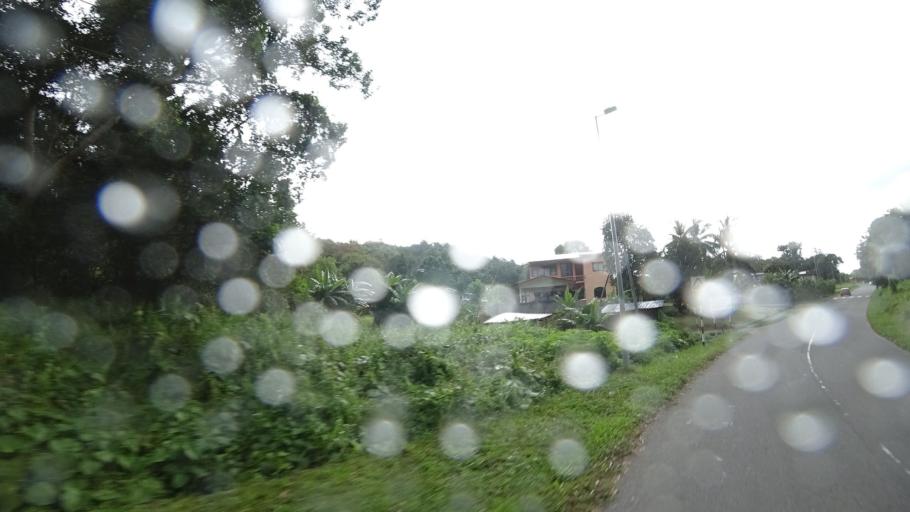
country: BN
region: Brunei and Muara
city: Bandar Seri Begawan
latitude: 4.8656
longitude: 114.9438
